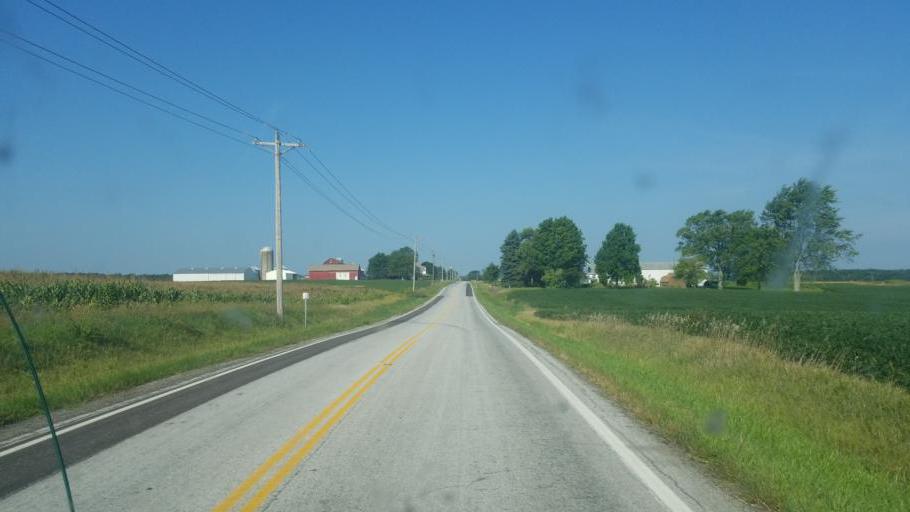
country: US
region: Ohio
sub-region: Lorain County
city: Wellington
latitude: 41.1004
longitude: -82.1509
